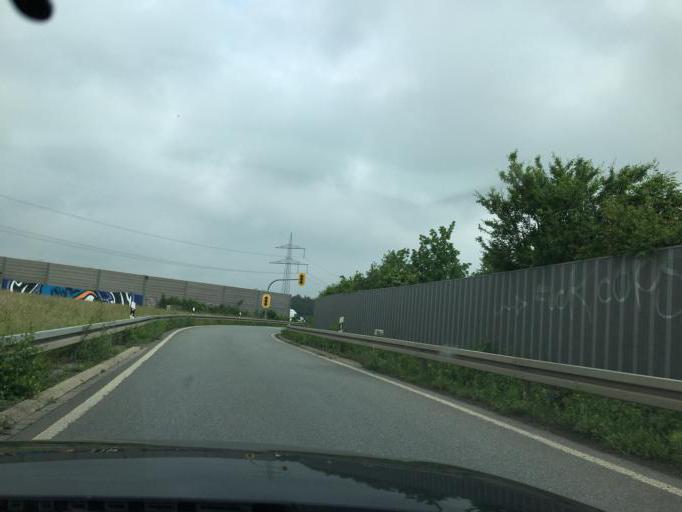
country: DE
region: North Rhine-Westphalia
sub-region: Regierungsbezirk Munster
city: Gelsenkirchen
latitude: 51.5342
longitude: 7.0973
